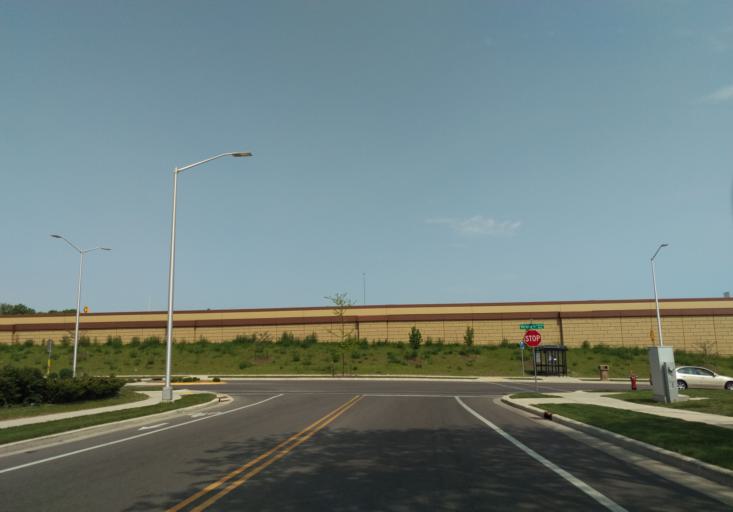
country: US
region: Wisconsin
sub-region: Dane County
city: Shorewood Hills
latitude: 43.0323
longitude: -89.4576
